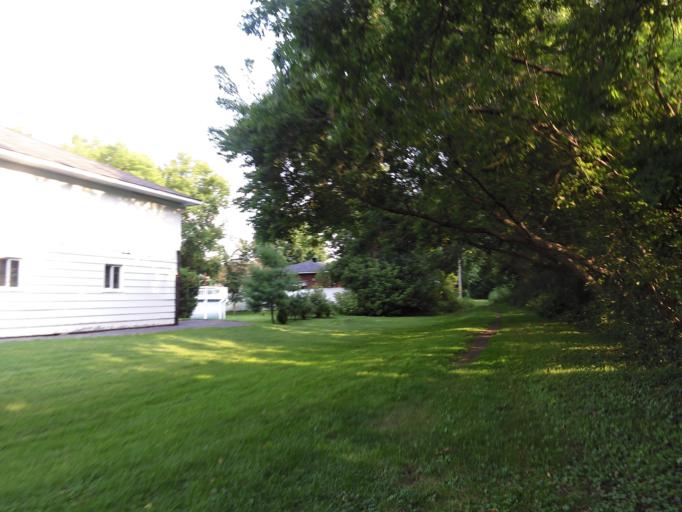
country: CA
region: Ontario
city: Bells Corners
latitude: 45.3965
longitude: -75.8542
